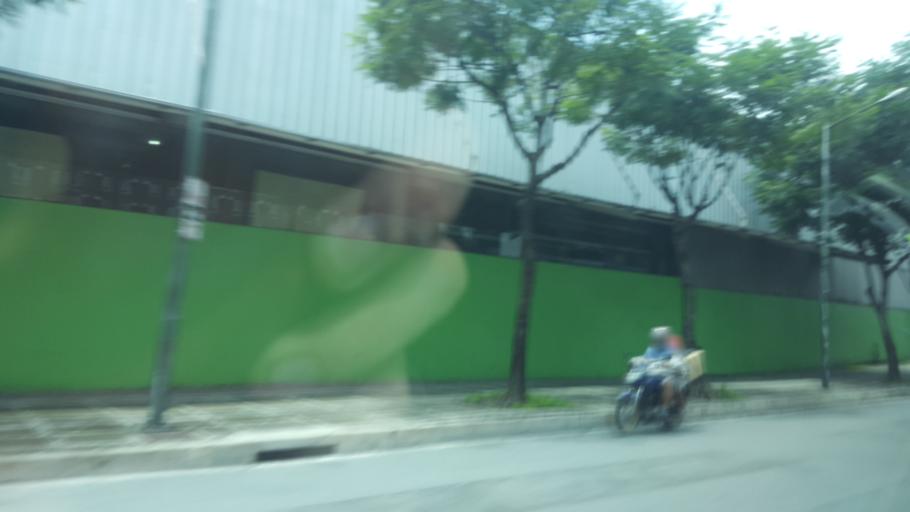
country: PH
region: Metro Manila
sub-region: Makati City
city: Makati City
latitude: 14.5555
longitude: 121.0507
